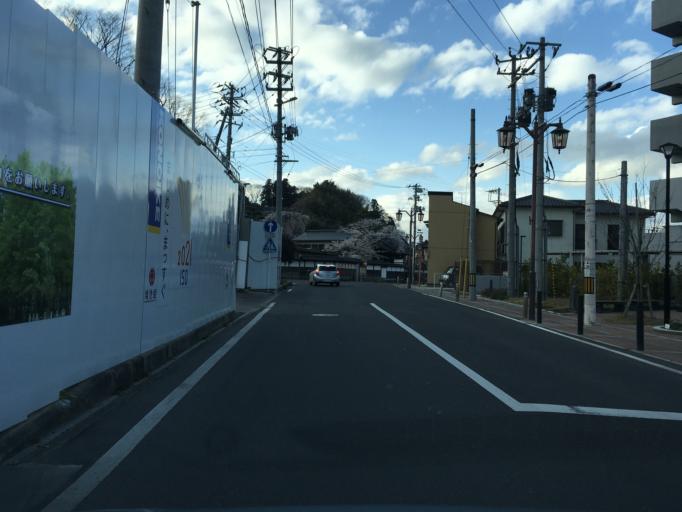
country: JP
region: Miyagi
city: Ishinomaki
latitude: 38.4288
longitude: 141.3060
